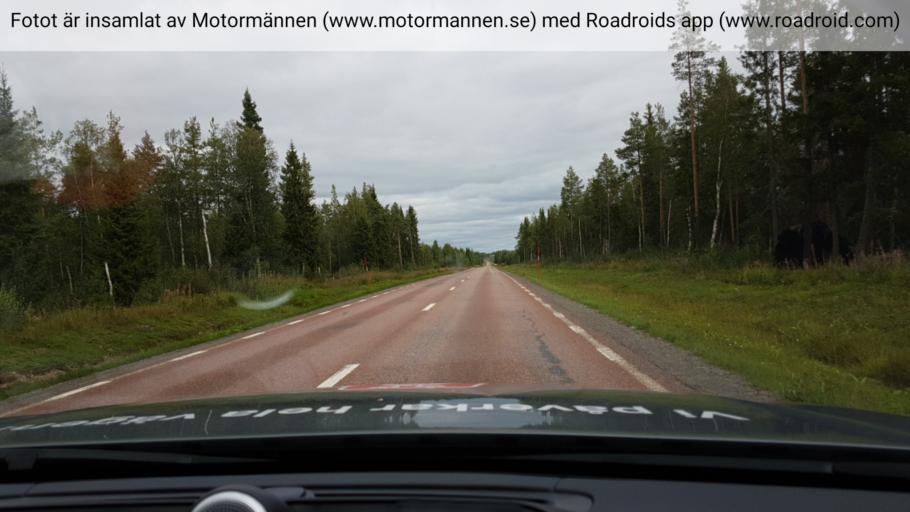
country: SE
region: Jaemtland
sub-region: Stroemsunds Kommun
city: Stroemsund
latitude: 63.7920
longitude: 15.5134
